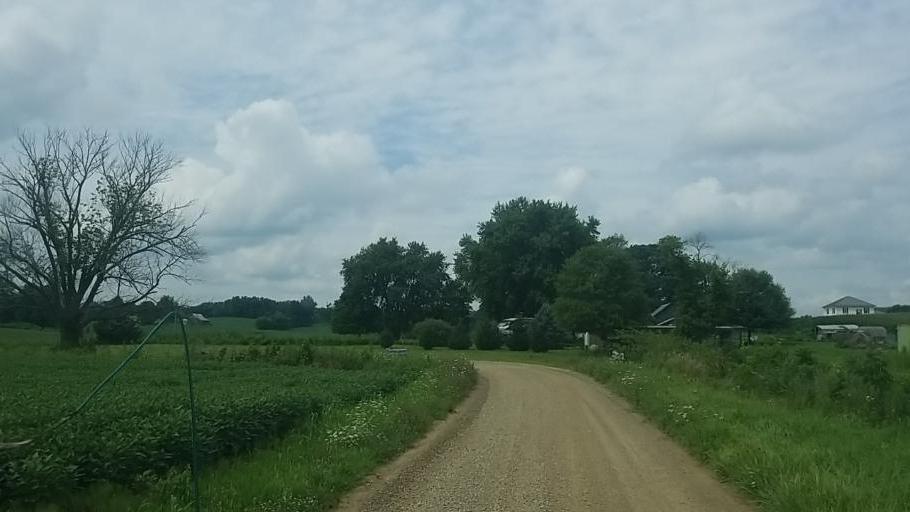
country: US
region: Ohio
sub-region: Knox County
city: Gambier
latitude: 40.3126
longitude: -82.3753
